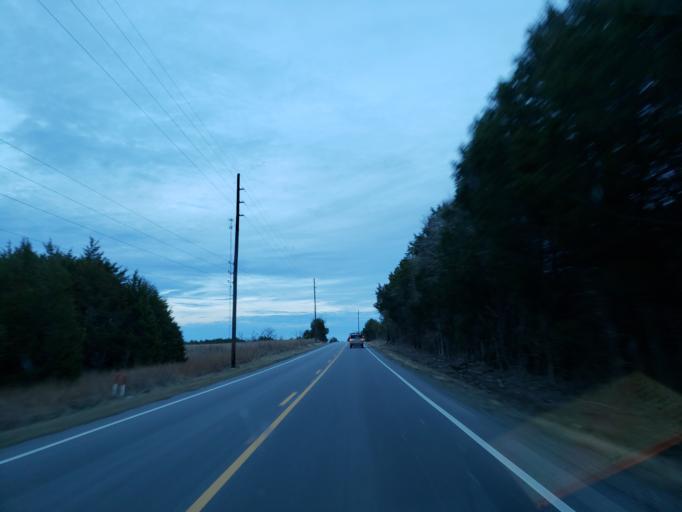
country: US
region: Alabama
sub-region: Sumter County
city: Livingston
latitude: 32.8070
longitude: -88.2979
